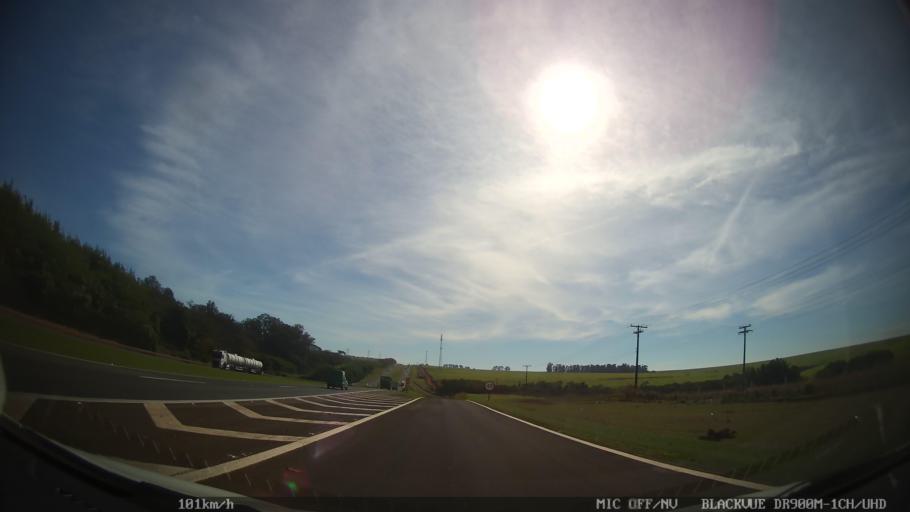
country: BR
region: Sao Paulo
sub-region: Araras
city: Araras
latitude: -22.2764
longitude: -47.3923
